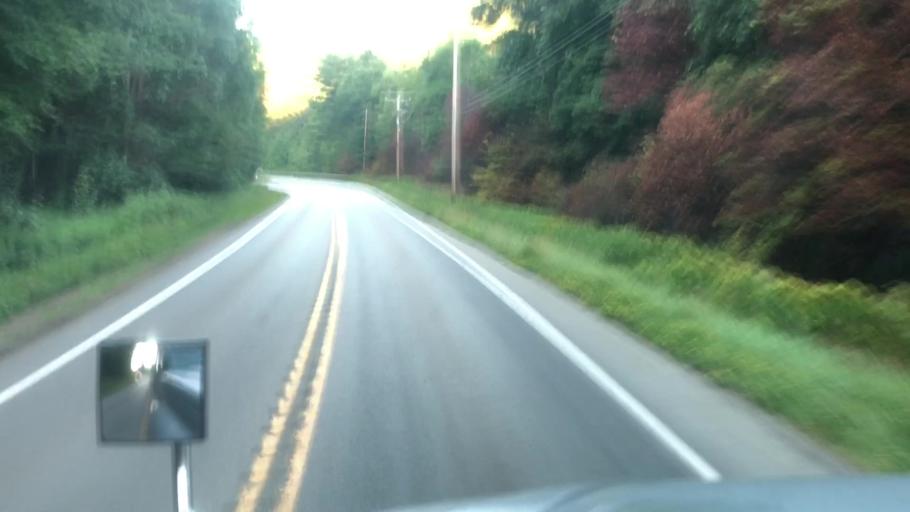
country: US
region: Pennsylvania
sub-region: Venango County
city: Hasson Heights
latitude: 41.4828
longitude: -79.6723
